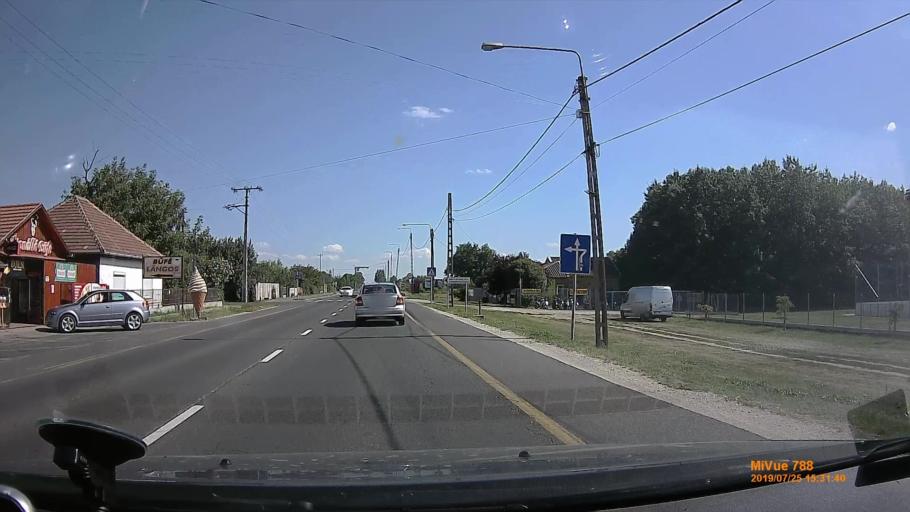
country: HU
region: Borsod-Abauj-Zemplen
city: Malyi
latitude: 48.0120
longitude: 20.8251
